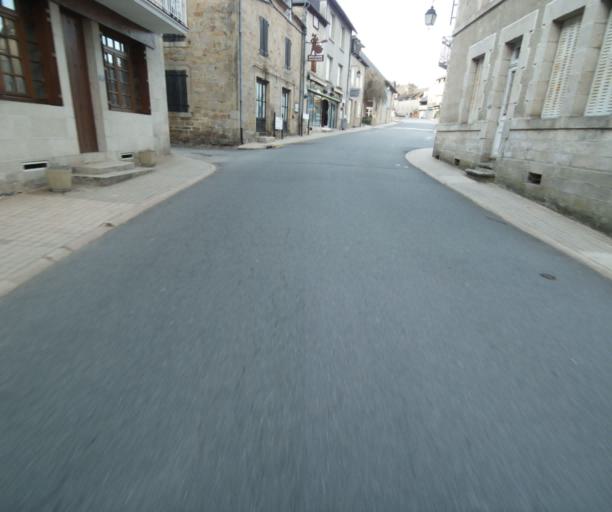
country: FR
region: Limousin
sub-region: Departement de la Correze
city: Correze
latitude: 45.3712
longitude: 1.8737
